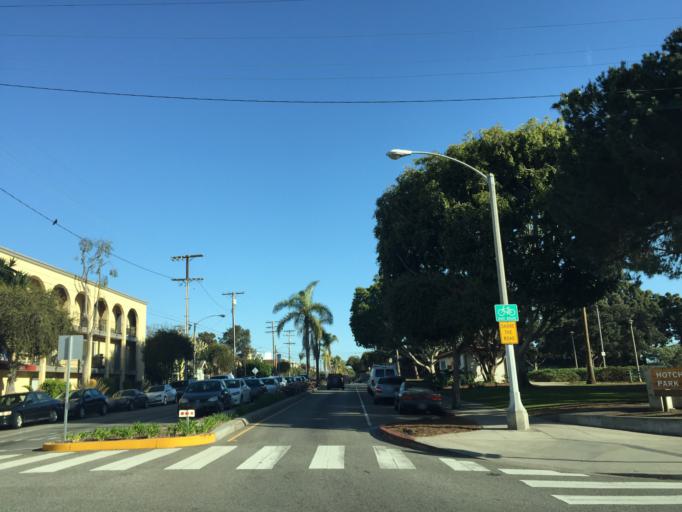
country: US
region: California
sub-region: Los Angeles County
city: Santa Monica
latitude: 34.0065
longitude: -118.4842
